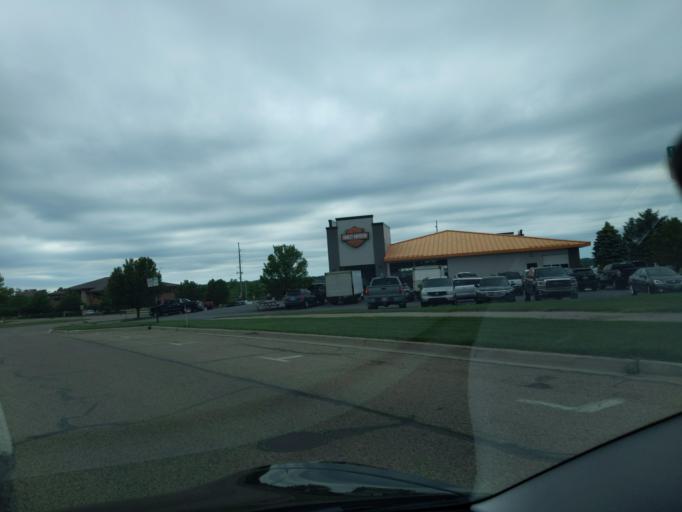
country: US
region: Michigan
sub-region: Muskegon County
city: Muskegon
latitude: 43.2387
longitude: -86.2489
